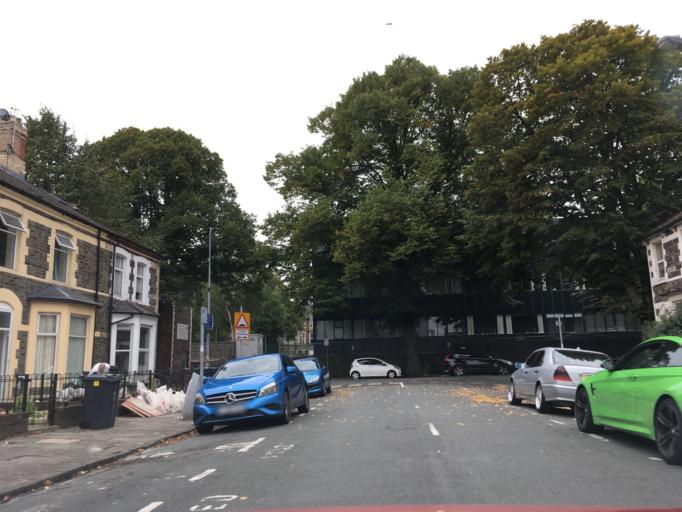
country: GB
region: Wales
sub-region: Cardiff
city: Cardiff
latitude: 51.4875
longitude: -3.1744
